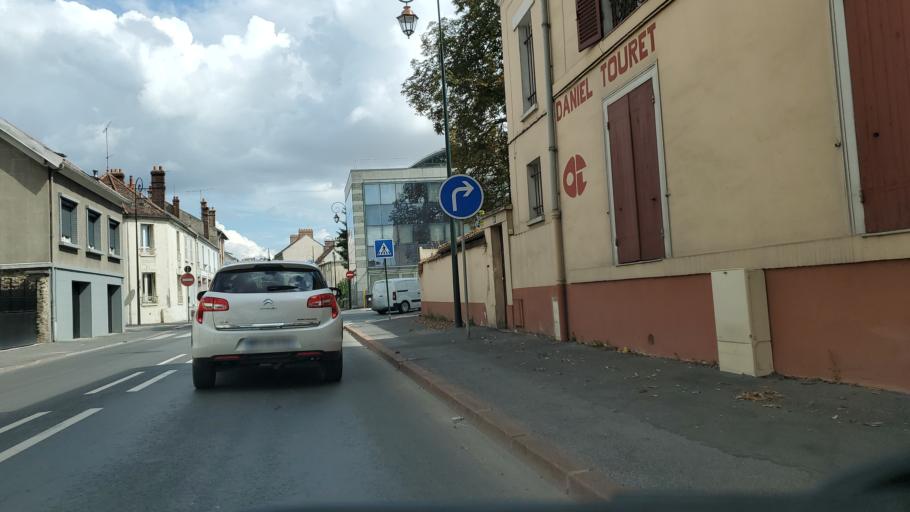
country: FR
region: Ile-de-France
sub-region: Departement de Seine-et-Marne
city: Coulommiers
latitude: 48.8115
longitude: 3.0792
